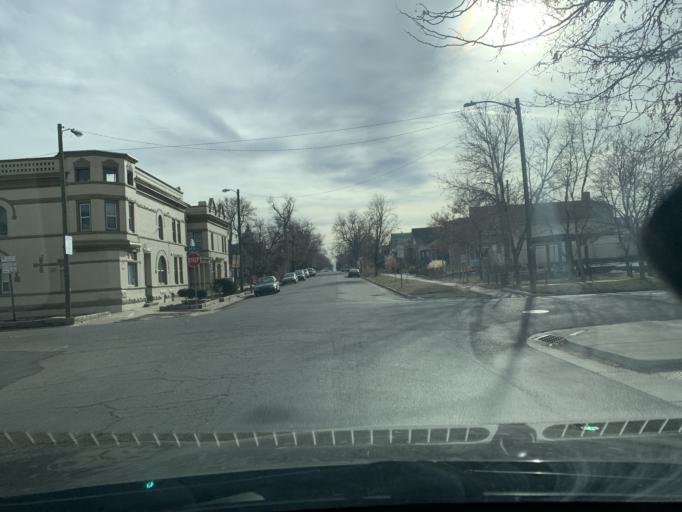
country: US
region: Colorado
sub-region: Denver County
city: Denver
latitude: 39.7387
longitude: -105.0016
